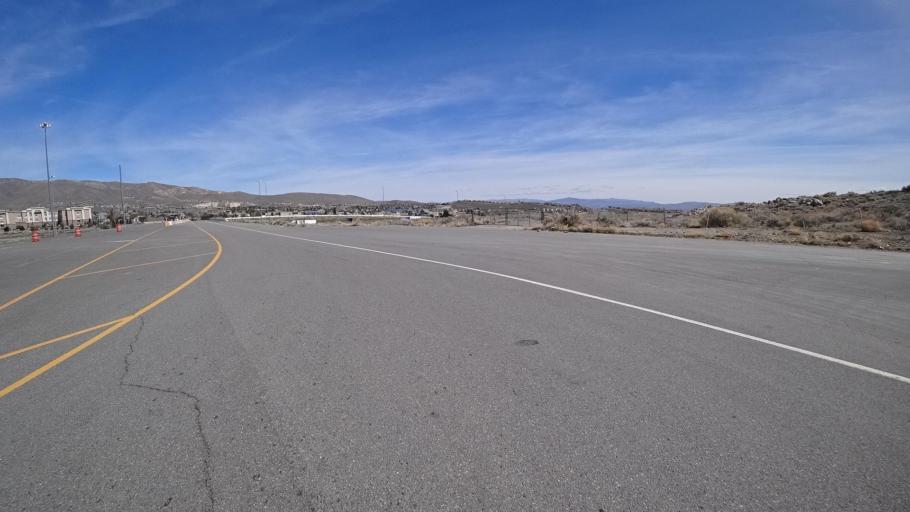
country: US
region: Nevada
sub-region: Washoe County
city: Mogul
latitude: 39.5139
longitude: -119.8873
